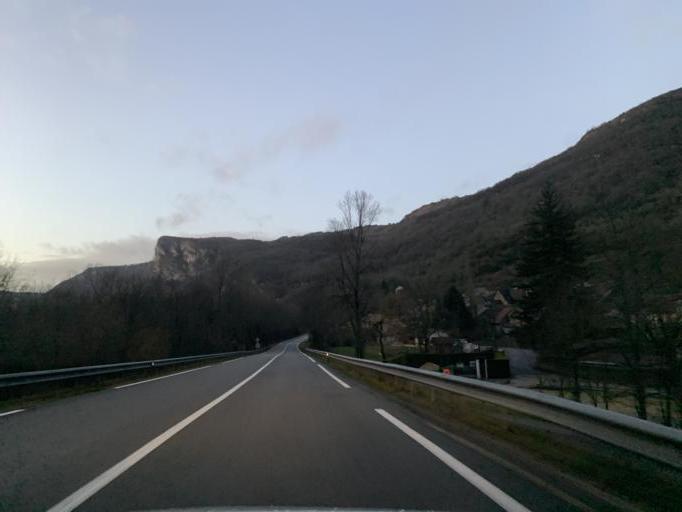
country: FR
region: Rhone-Alpes
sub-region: Departement de l'Ain
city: Virieu-le-Grand
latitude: 45.8307
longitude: 5.5929
